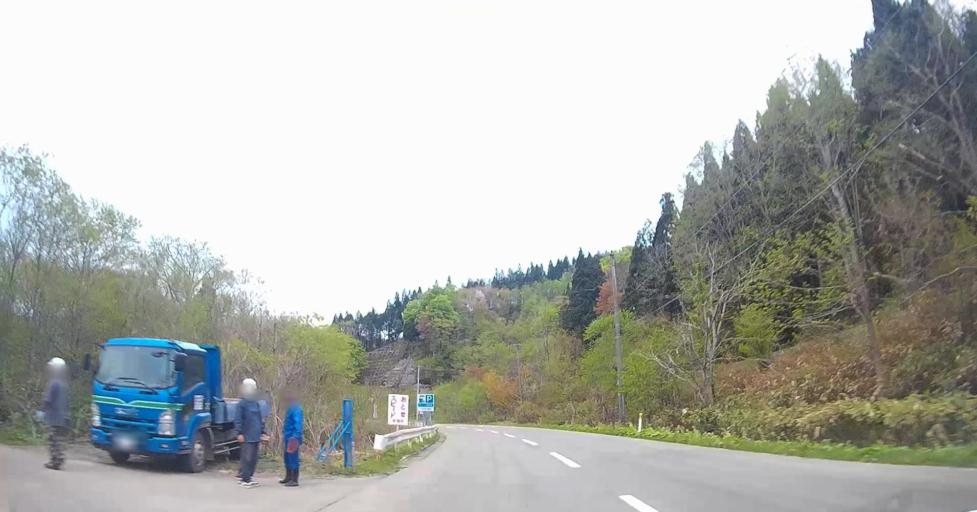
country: JP
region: Aomori
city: Goshogawara
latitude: 41.1191
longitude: 140.5236
